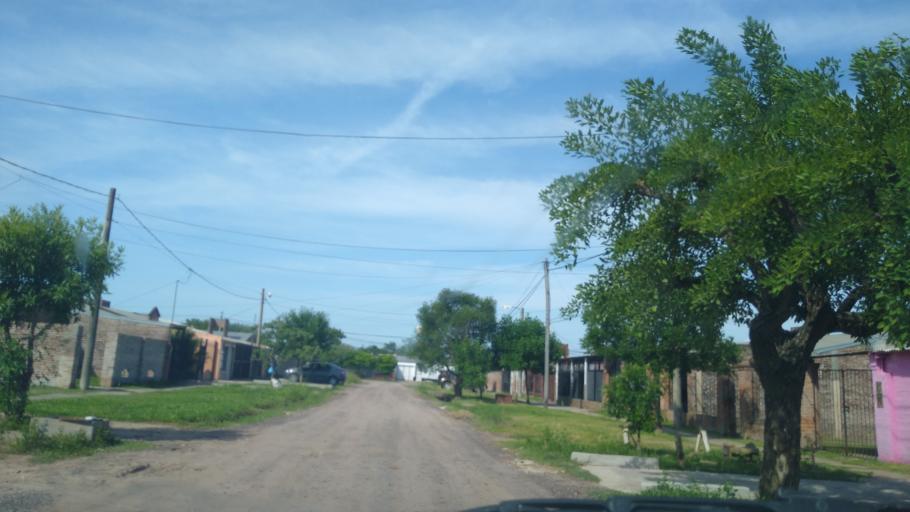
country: AR
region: Chaco
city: Puerto Vilelas
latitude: -27.4979
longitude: -58.9615
